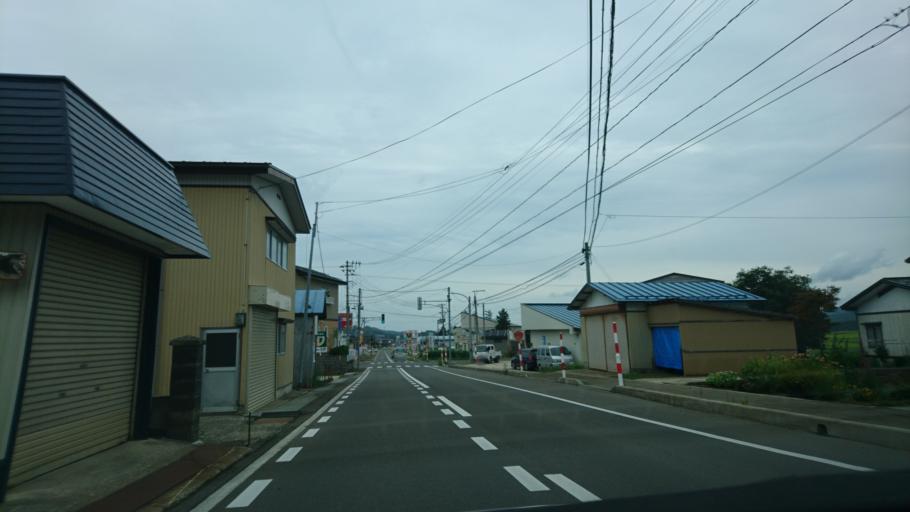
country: JP
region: Akita
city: Yuzawa
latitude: 39.1461
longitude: 140.5747
